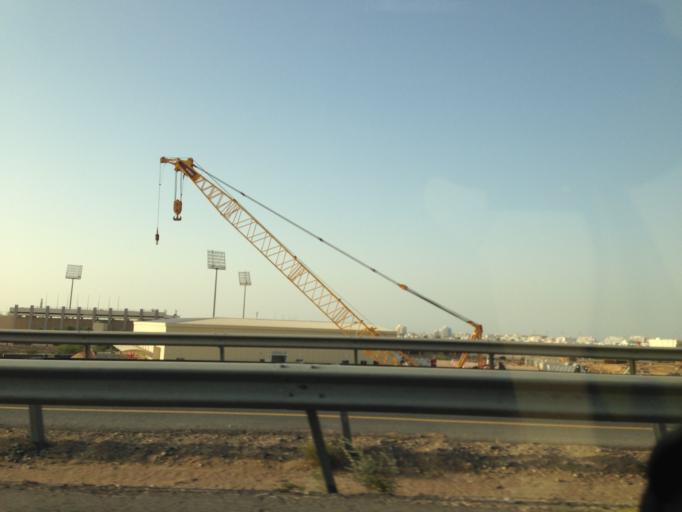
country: OM
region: Muhafazat Masqat
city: Bawshar
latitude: 23.5692
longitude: 58.4022
